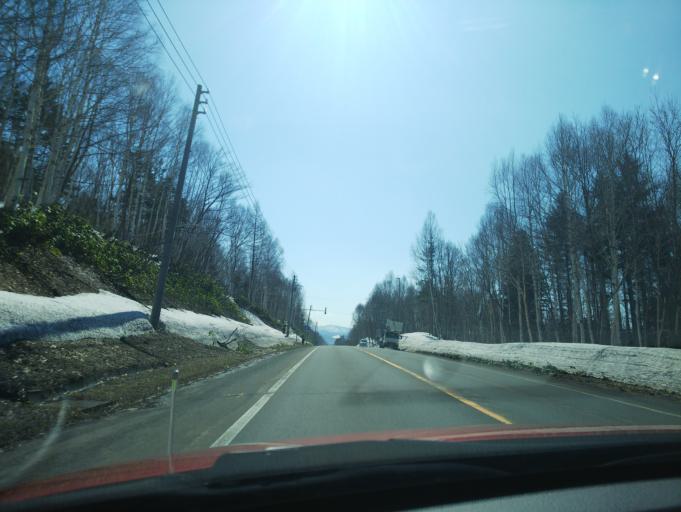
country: JP
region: Hokkaido
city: Nayoro
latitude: 44.6417
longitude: 142.2698
